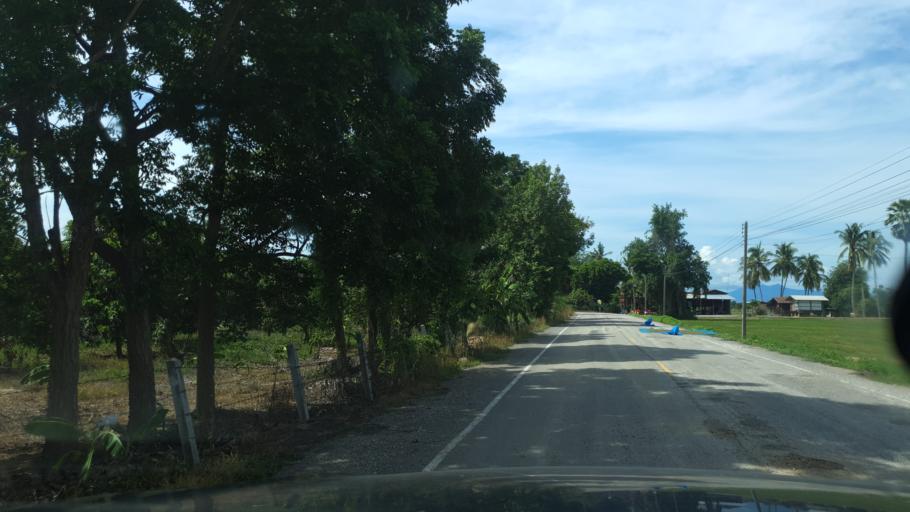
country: TH
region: Sukhothai
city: Si Samrong
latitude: 17.2001
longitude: 99.7214
